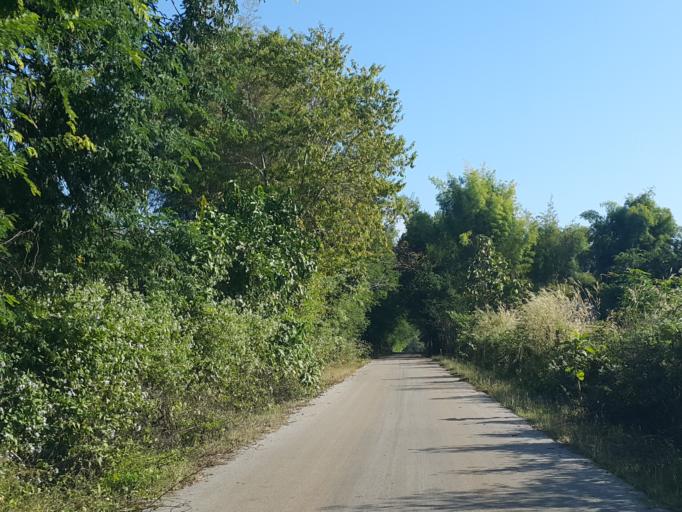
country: TH
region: Lampang
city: Mae Mo
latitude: 18.2977
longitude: 99.6620
